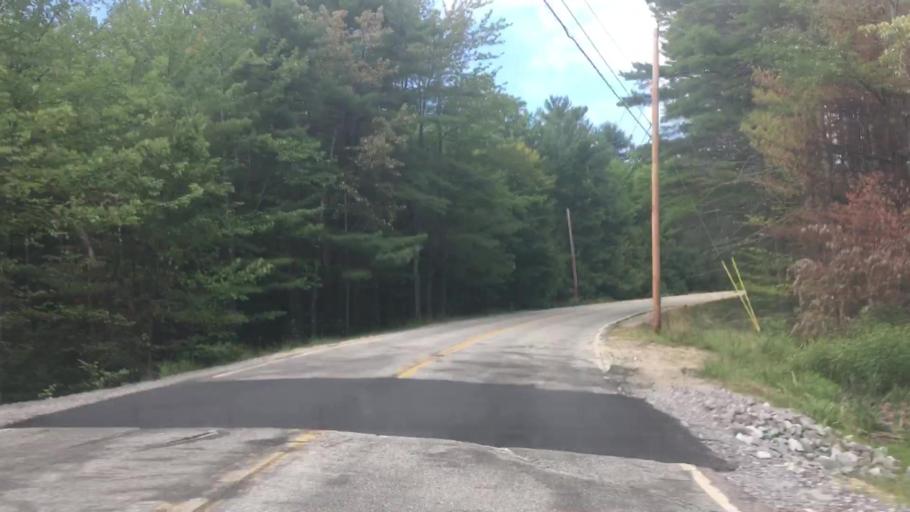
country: US
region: Maine
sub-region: Oxford County
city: Oxford
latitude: 44.0775
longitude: -70.5494
